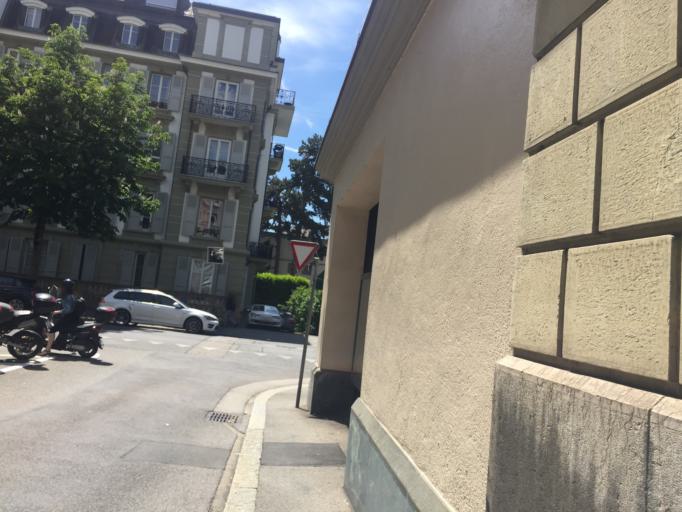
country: CH
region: Vaud
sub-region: Lausanne District
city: Lausanne
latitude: 46.5153
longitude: 6.6310
